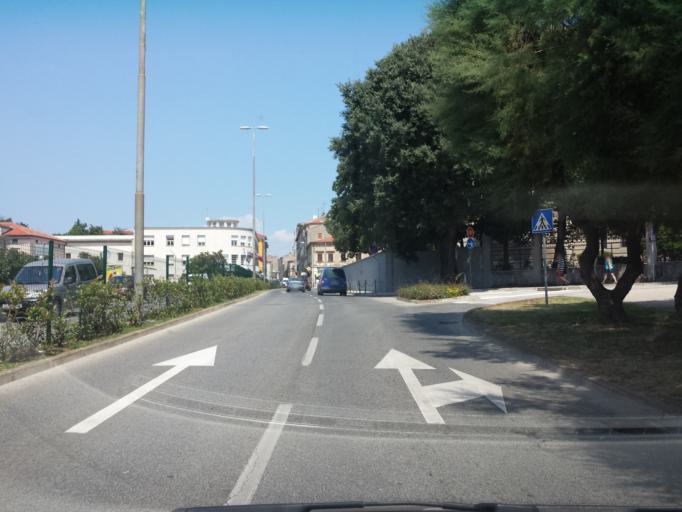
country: HR
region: Istarska
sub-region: Grad Pula
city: Pula
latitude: 44.8660
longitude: 13.8503
